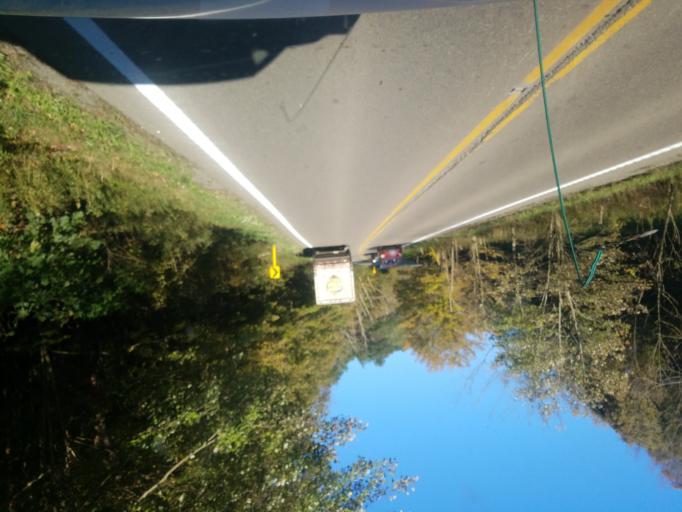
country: US
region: Ohio
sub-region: Columbiana County
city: New Waterford
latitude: 40.7715
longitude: -80.6284
